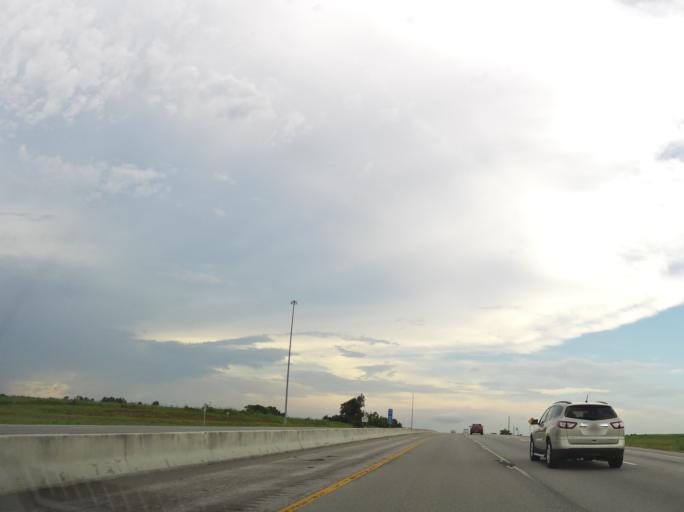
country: US
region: Kentucky
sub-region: Madison County
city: Richmond
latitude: 37.6761
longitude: -84.3120
